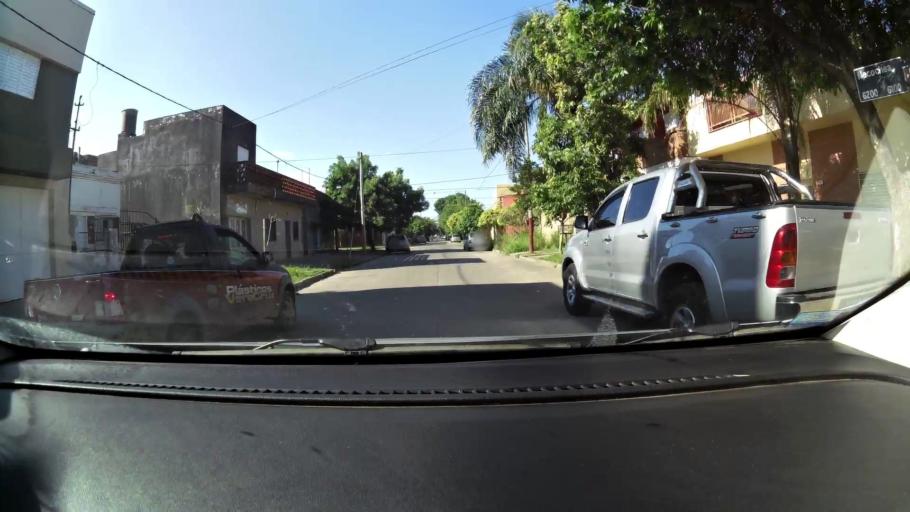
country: AR
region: Santa Fe
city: Santa Fe de la Vera Cruz
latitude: -31.6133
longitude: -60.6873
